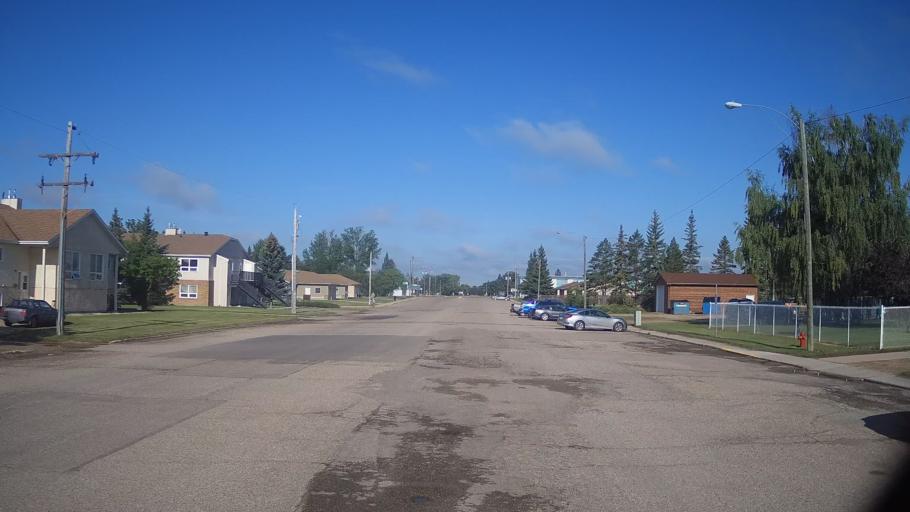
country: CA
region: Saskatchewan
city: Lanigan
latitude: 51.8508
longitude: -105.0253
